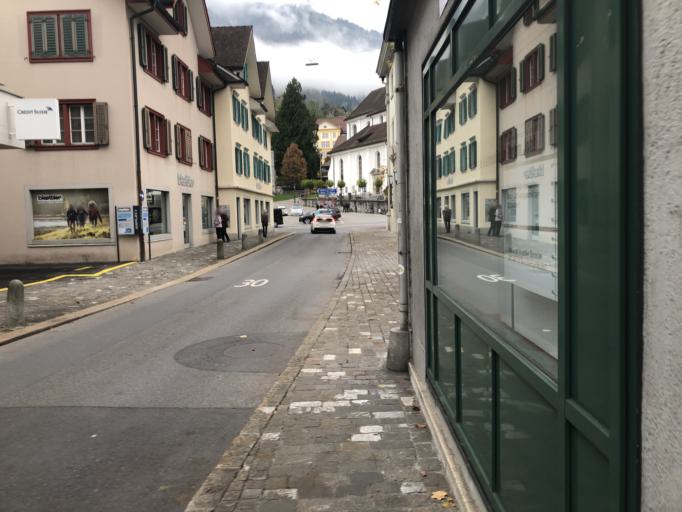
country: CH
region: Nidwalden
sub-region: Nidwalden
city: Stans
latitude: 46.9576
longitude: 8.3666
